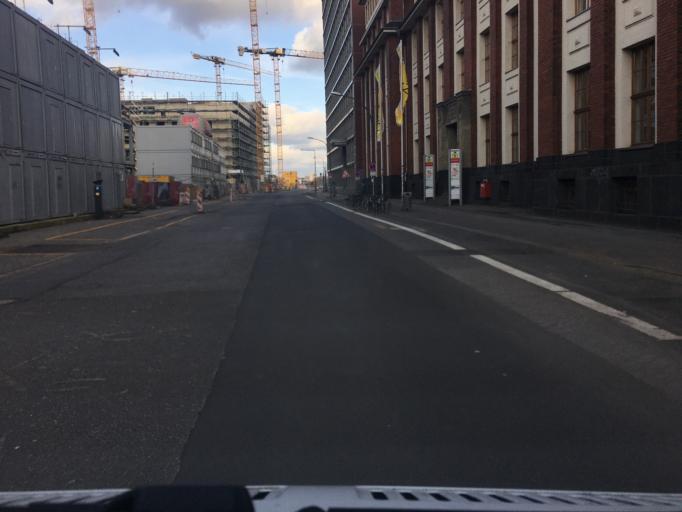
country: DE
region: North Rhine-Westphalia
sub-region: Regierungsbezirk Koln
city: Muelheim
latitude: 50.9678
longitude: 7.0110
